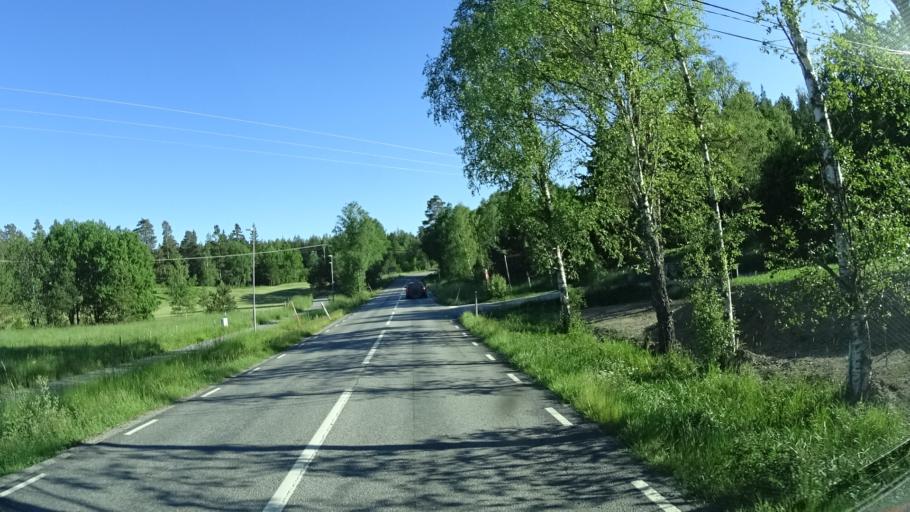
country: SE
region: Stockholm
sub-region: Vallentuna Kommun
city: Vallentuna
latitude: 59.5589
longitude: 18.1026
